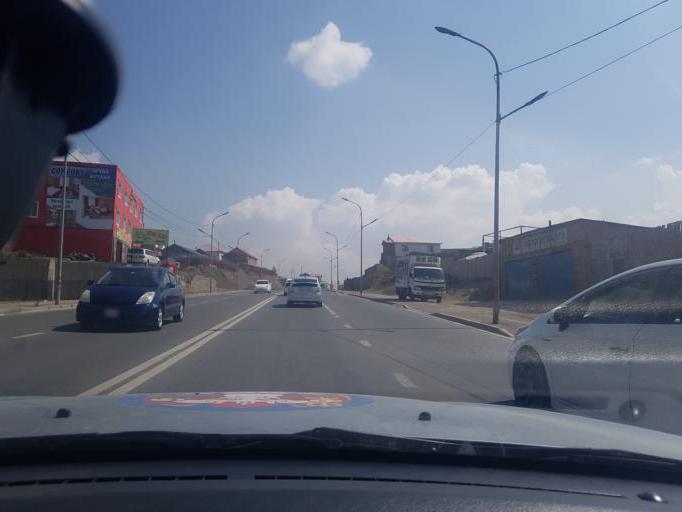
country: MN
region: Ulaanbaatar
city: Ulaanbaatar
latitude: 47.9557
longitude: 106.8461
